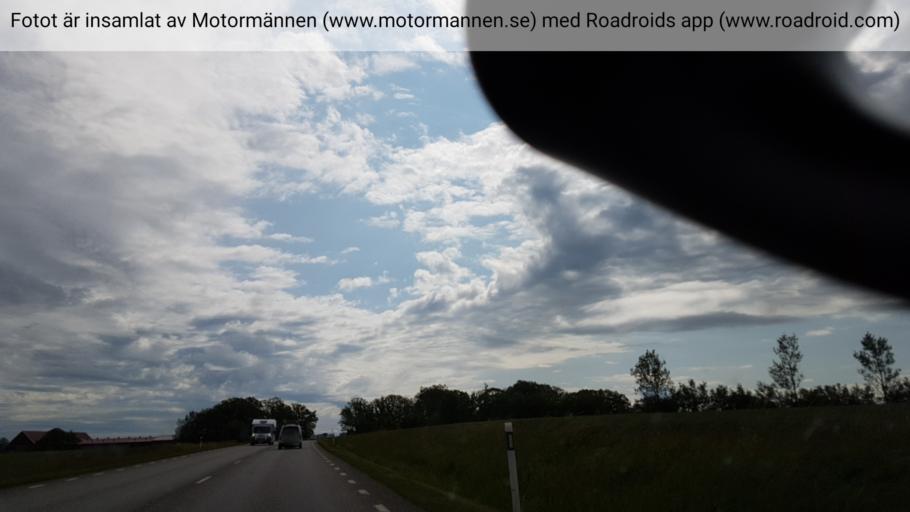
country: SE
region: Vaestra Goetaland
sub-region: Vara Kommun
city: Vara
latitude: 58.3003
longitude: 12.9169
